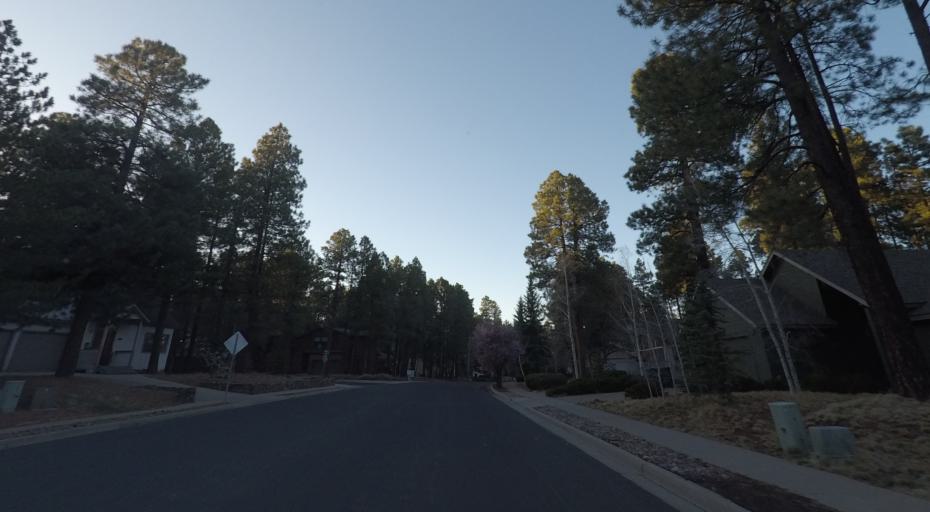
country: US
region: Arizona
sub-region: Coconino County
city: Flagstaff
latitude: 35.1738
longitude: -111.6791
